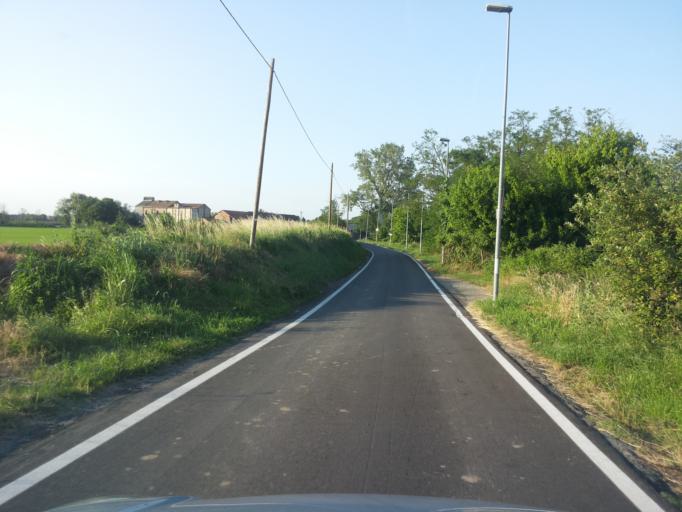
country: IT
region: Piedmont
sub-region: Provincia di Vercelli
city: Vercelli
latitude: 45.2971
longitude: 8.4407
